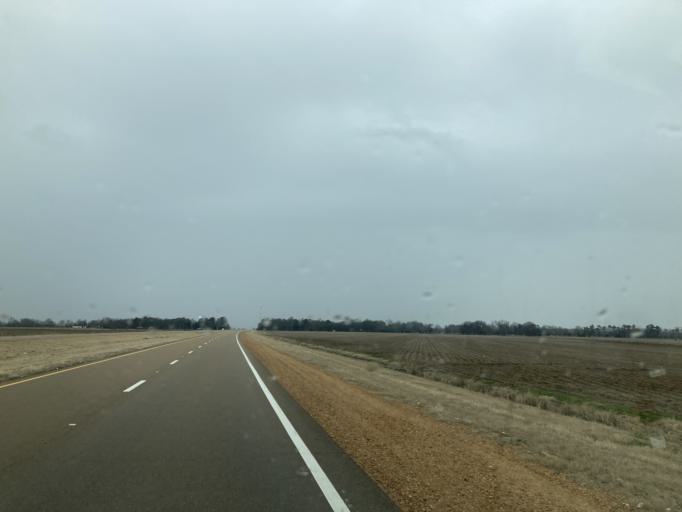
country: US
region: Mississippi
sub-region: Humphreys County
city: Belzoni
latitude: 33.0846
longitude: -90.4855
